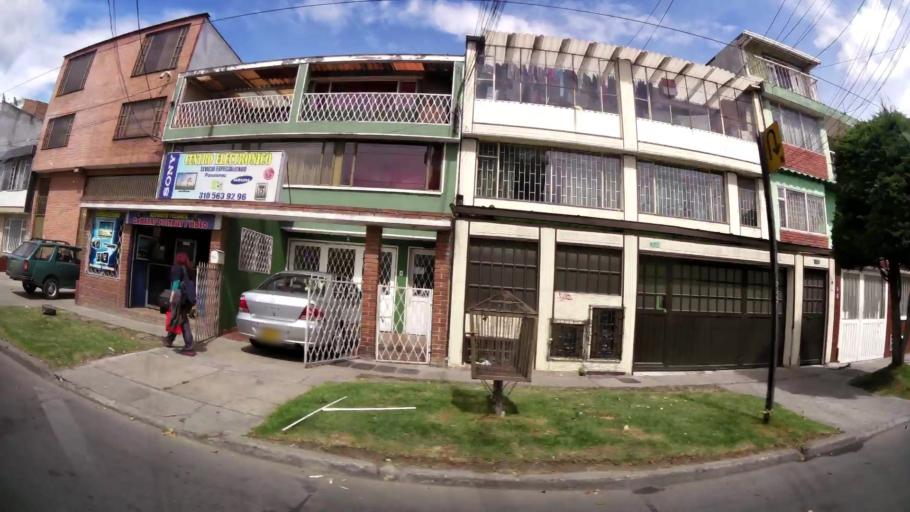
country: CO
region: Bogota D.C.
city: Bogota
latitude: 4.6264
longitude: -74.1321
